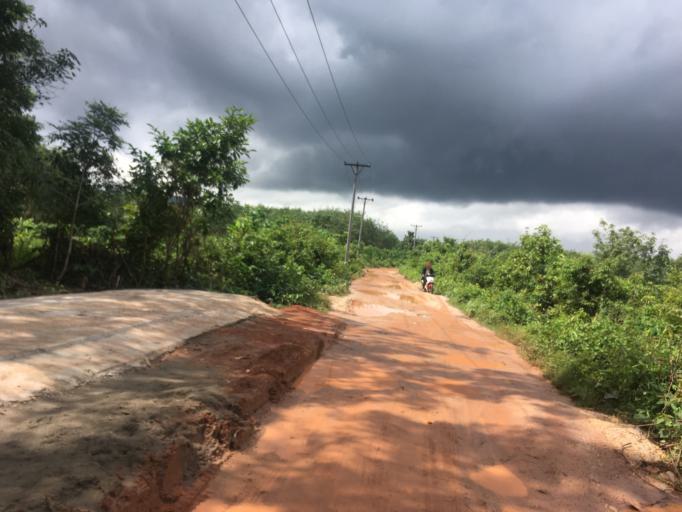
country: MM
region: Mon
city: Mawlamyine
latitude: 16.4597
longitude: 97.6891
